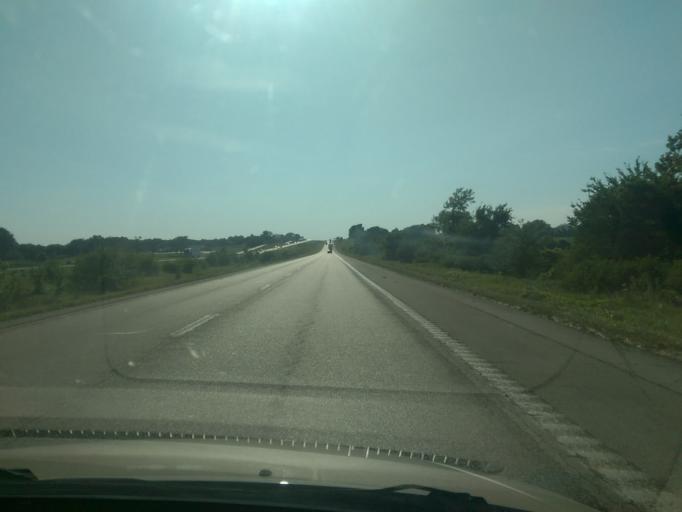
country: US
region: Missouri
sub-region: Lafayette County
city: Odessa
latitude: 39.0106
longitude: -94.0333
